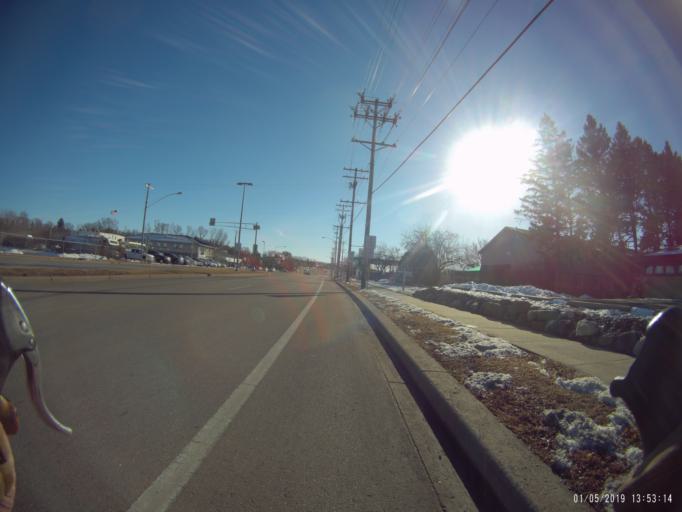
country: US
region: Wisconsin
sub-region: Dane County
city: Madison
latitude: 43.0441
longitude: -89.4041
